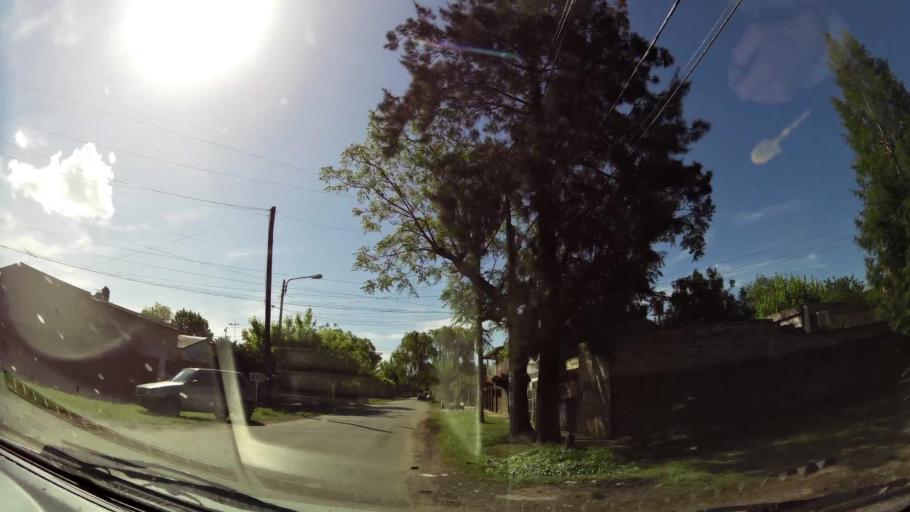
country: AR
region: Buenos Aires
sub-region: Partido de Quilmes
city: Quilmes
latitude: -34.7982
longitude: -58.2482
